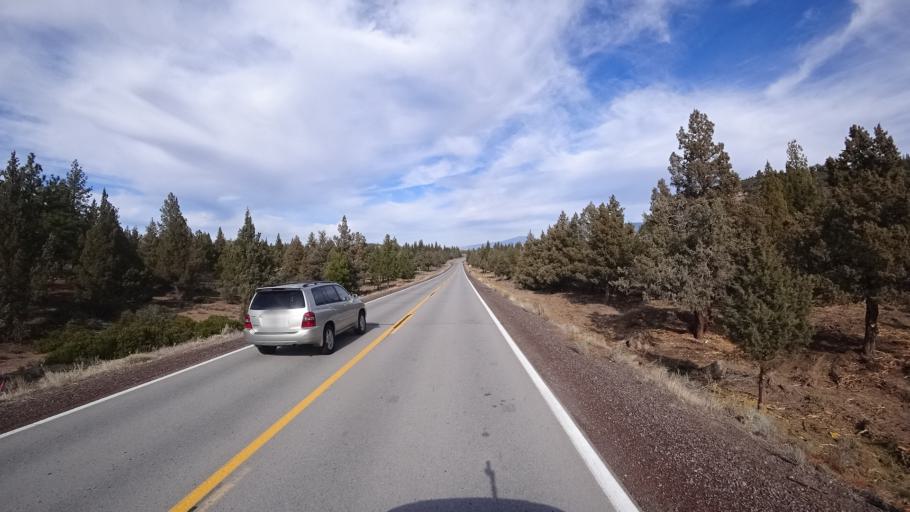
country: US
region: California
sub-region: Siskiyou County
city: Weed
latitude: 41.5204
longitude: -122.3664
